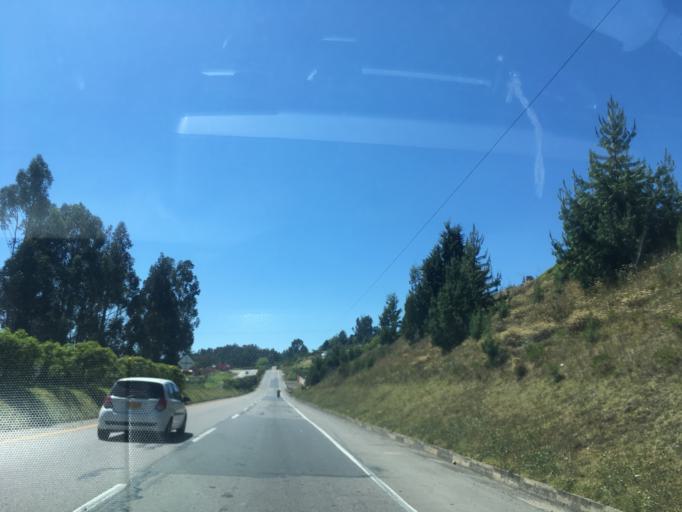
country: CO
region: Boyaca
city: Tuta
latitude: 5.6861
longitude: -73.2655
